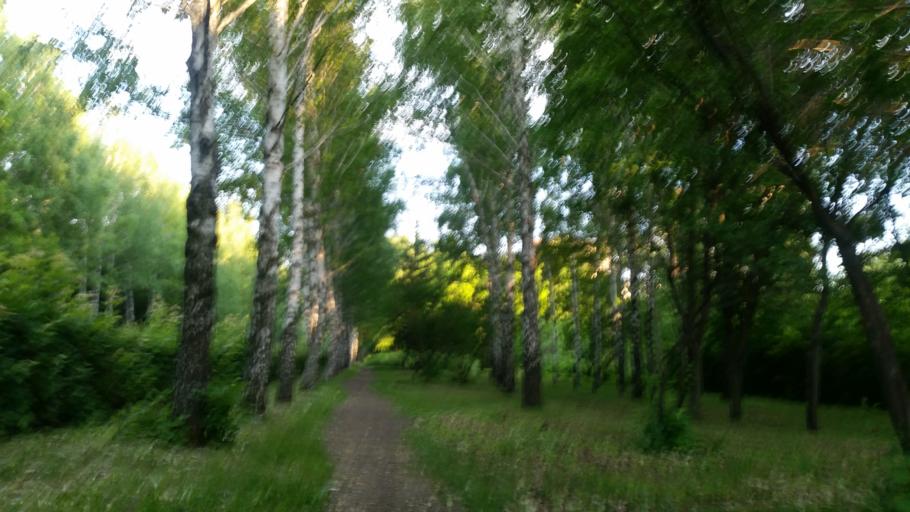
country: RU
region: Ulyanovsk
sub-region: Ulyanovskiy Rayon
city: Ulyanovsk
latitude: 54.3472
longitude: 48.3943
